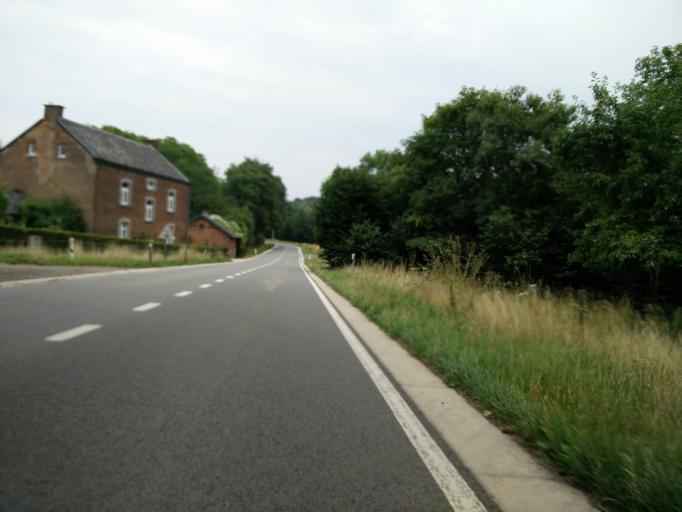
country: BE
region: Wallonia
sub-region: Province de Liege
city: Dalhem
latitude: 50.7133
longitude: 5.7613
